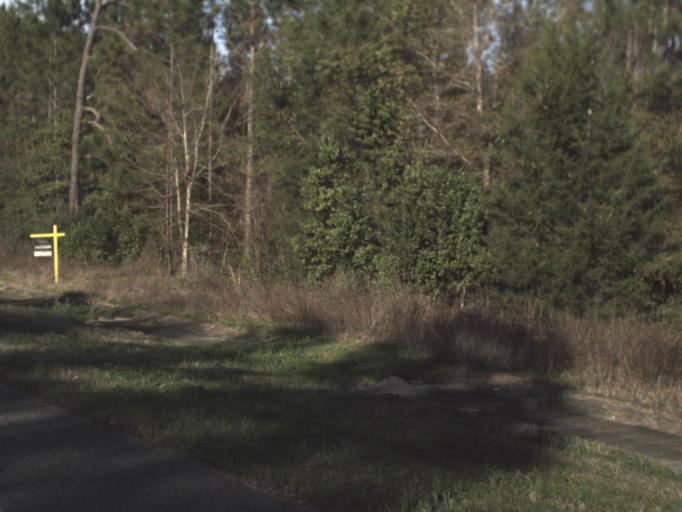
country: US
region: Florida
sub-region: Jackson County
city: Marianna
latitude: 30.6050
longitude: -85.1812
